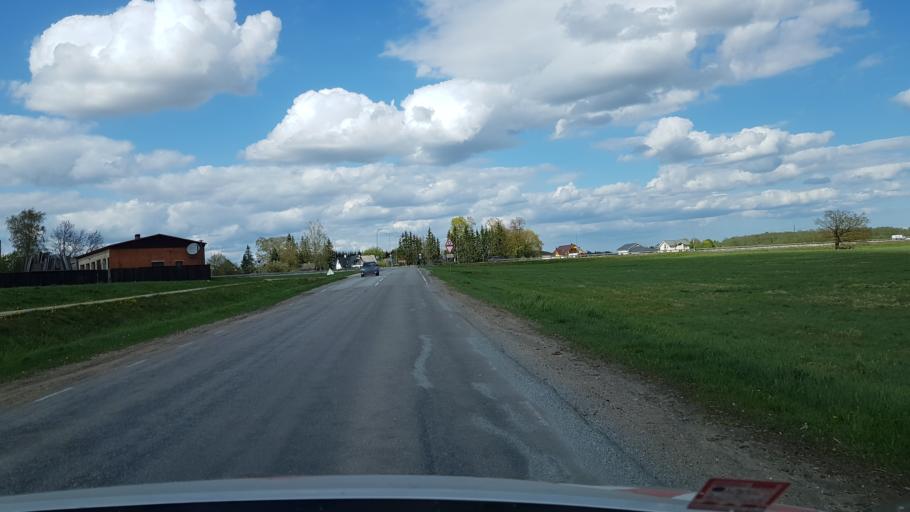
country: EE
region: Tartu
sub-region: Tartu linn
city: Tartu
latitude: 58.3704
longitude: 26.7989
